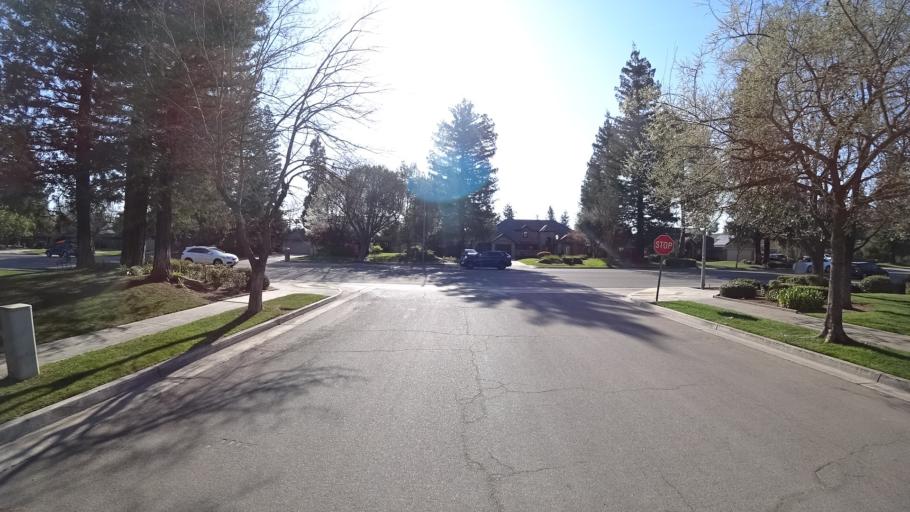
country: US
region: California
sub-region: Fresno County
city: Clovis
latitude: 36.8568
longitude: -119.7986
